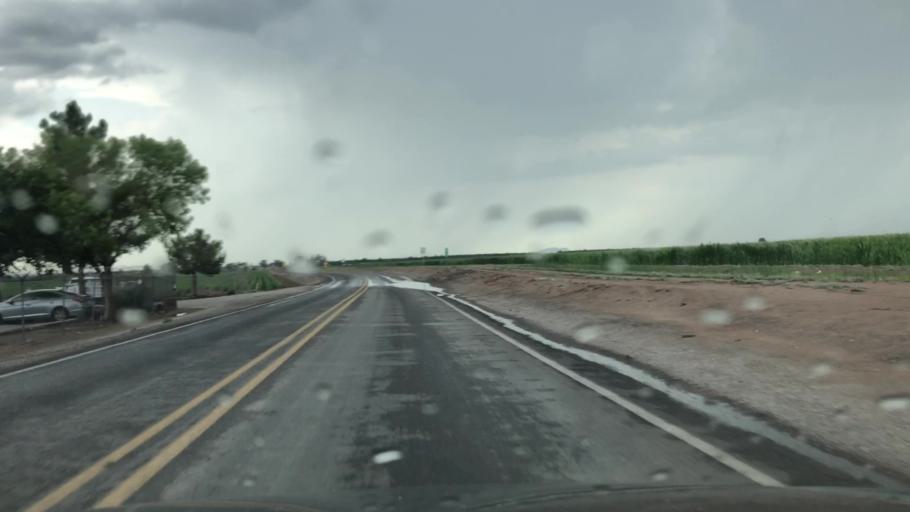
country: US
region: New Mexico
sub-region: Dona Ana County
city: Vado
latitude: 32.0618
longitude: -106.6774
